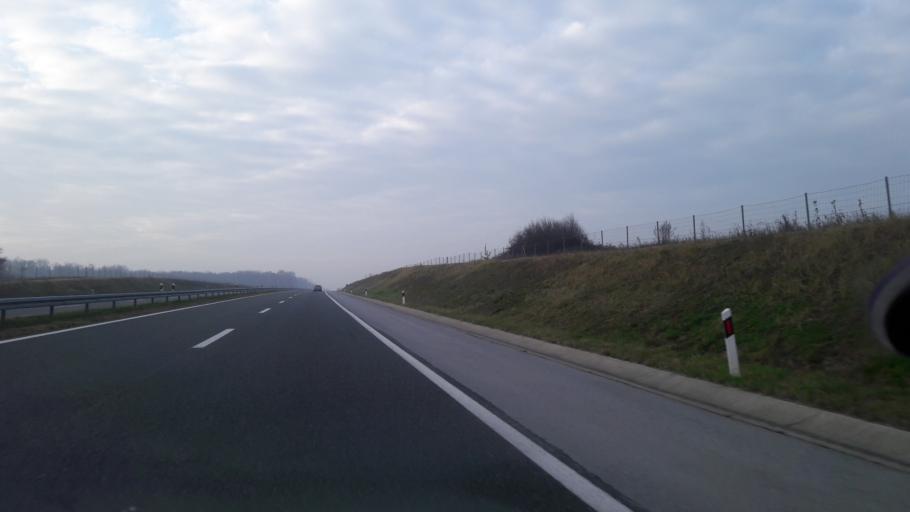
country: HR
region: Osjecko-Baranjska
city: Piskorevci
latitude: 45.2907
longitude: 18.3580
